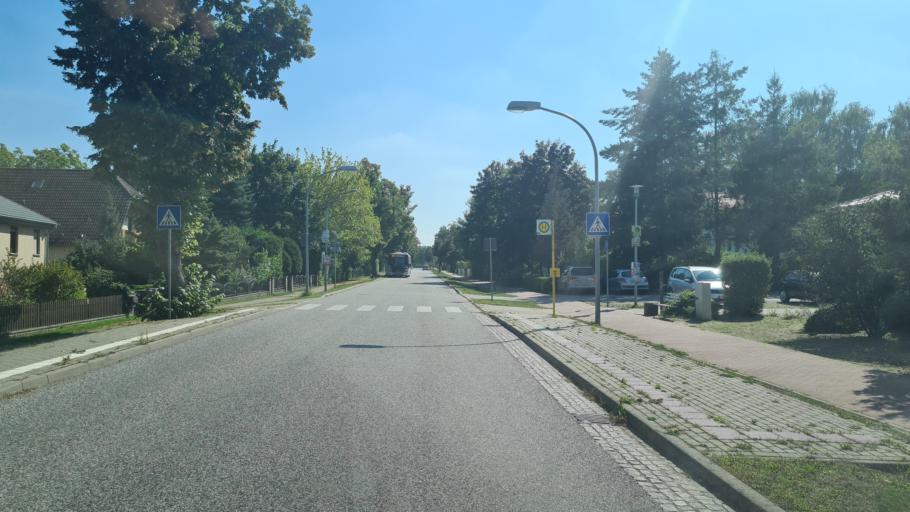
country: DE
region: Brandenburg
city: Paulinenaue
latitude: 52.6733
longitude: 12.7144
